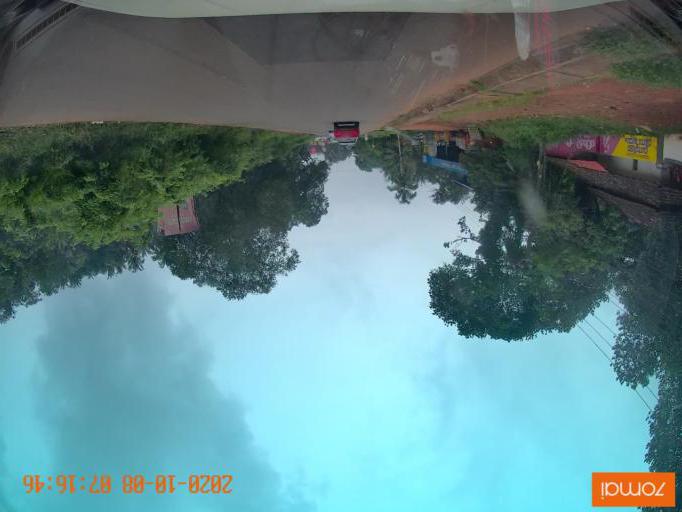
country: IN
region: Kerala
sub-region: Malappuram
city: Ponnani
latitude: 10.8333
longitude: 76.0183
